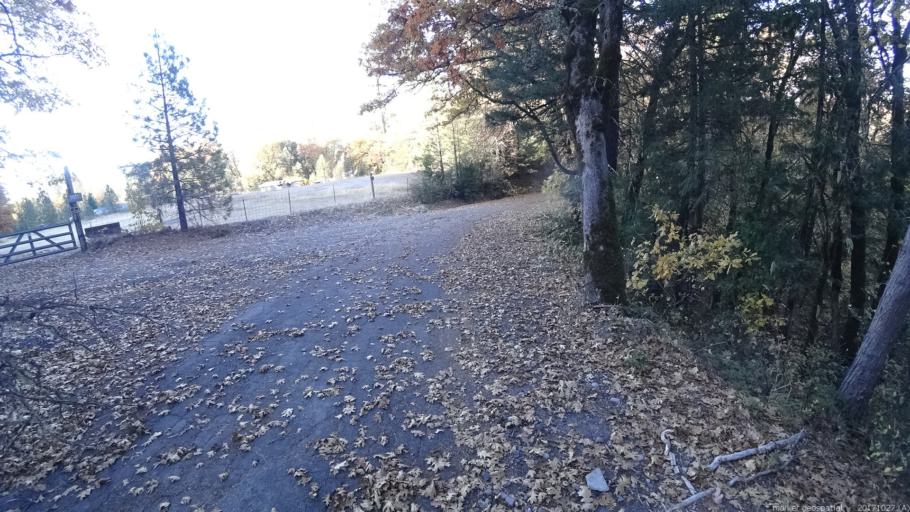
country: US
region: California
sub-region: Shasta County
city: Burney
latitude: 41.0242
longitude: -121.9026
